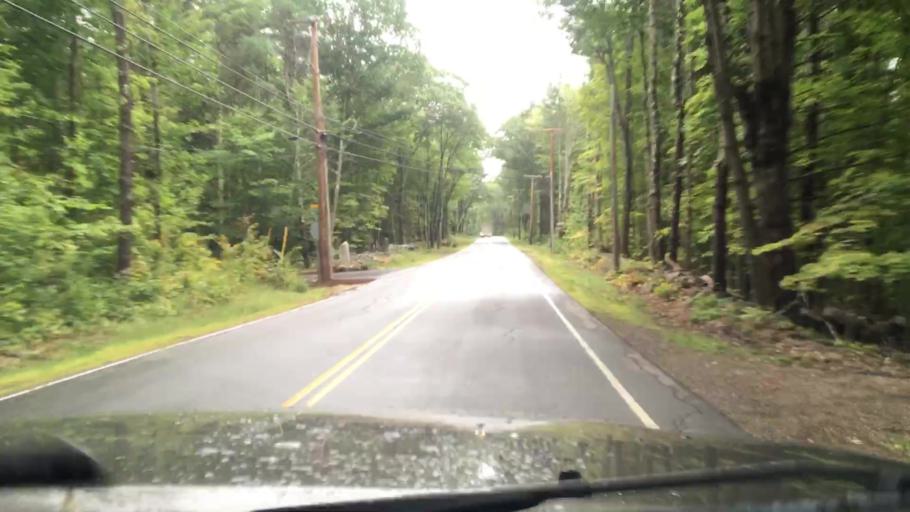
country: US
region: New Hampshire
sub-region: Belknap County
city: Meredith
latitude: 43.6440
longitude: -71.5348
